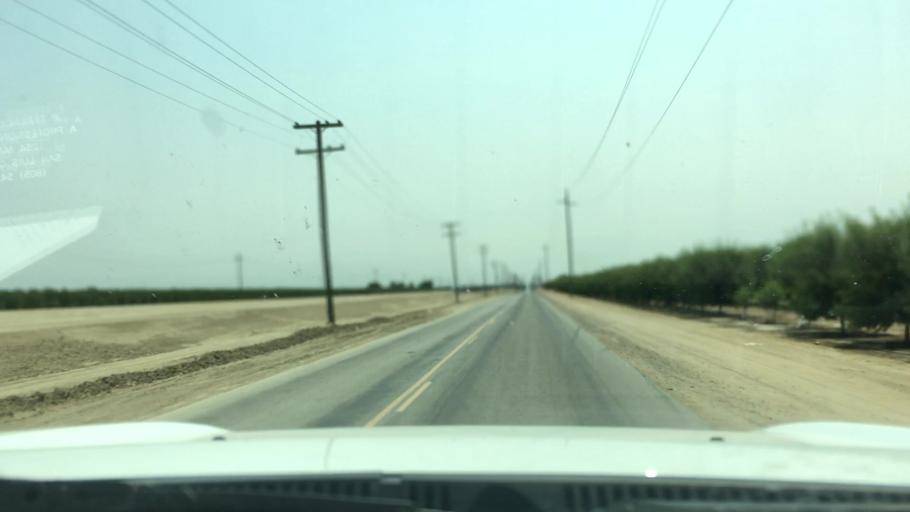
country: US
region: California
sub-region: Kern County
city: Wasco
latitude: 35.6156
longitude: -119.4379
